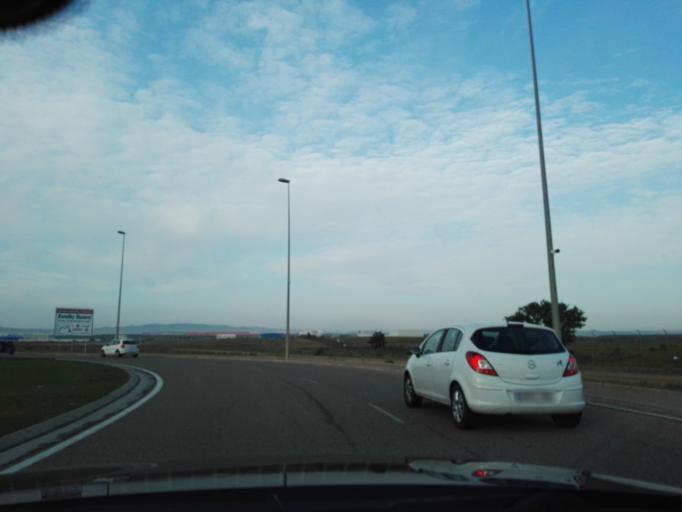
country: ES
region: Aragon
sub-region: Provincia de Zaragoza
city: Utebo
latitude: 41.6540
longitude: -1.0005
